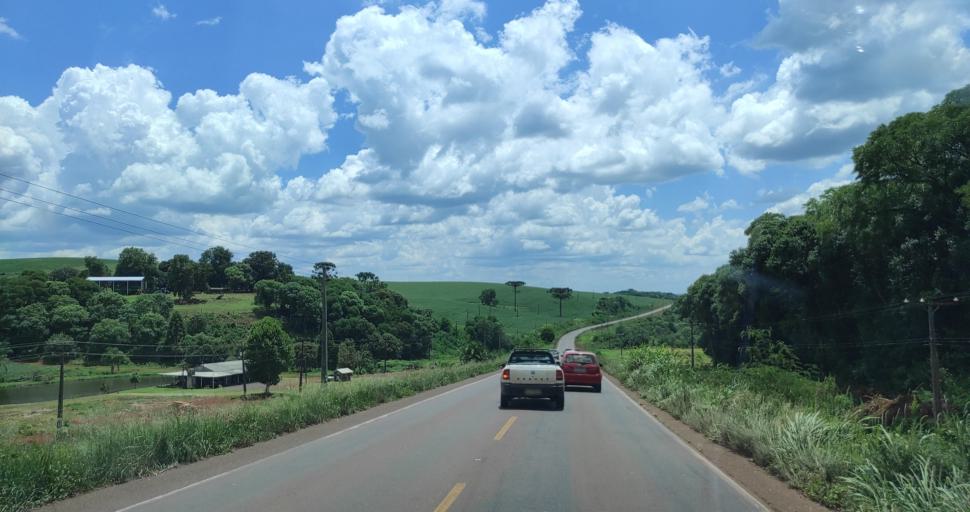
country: BR
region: Santa Catarina
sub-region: Xanxere
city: Xanxere
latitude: -26.8271
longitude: -52.4144
